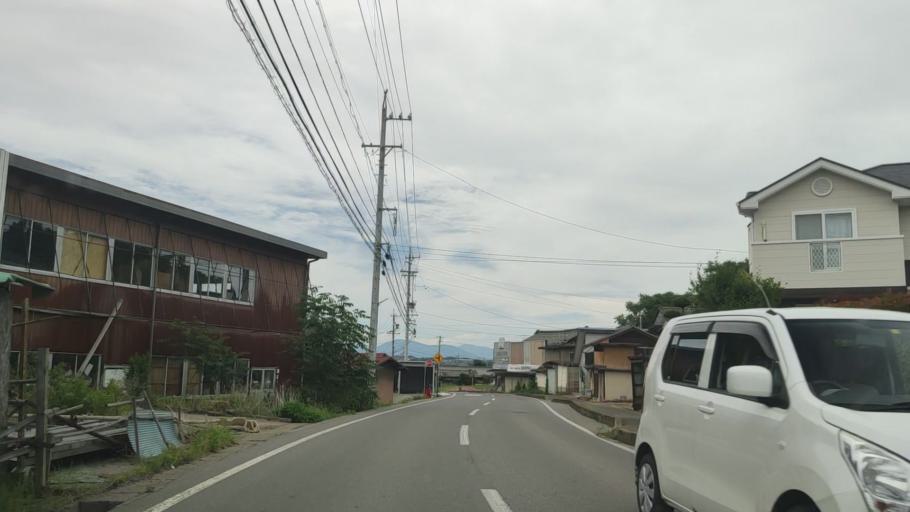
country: JP
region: Nagano
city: Kamimaruko
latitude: 36.2890
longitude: 138.3169
